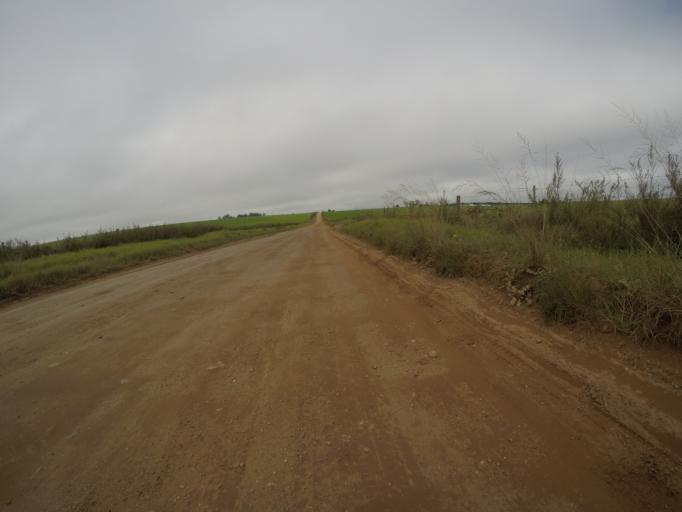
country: ZA
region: Eastern Cape
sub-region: Cacadu District Municipality
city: Kareedouw
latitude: -34.0254
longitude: 24.2415
